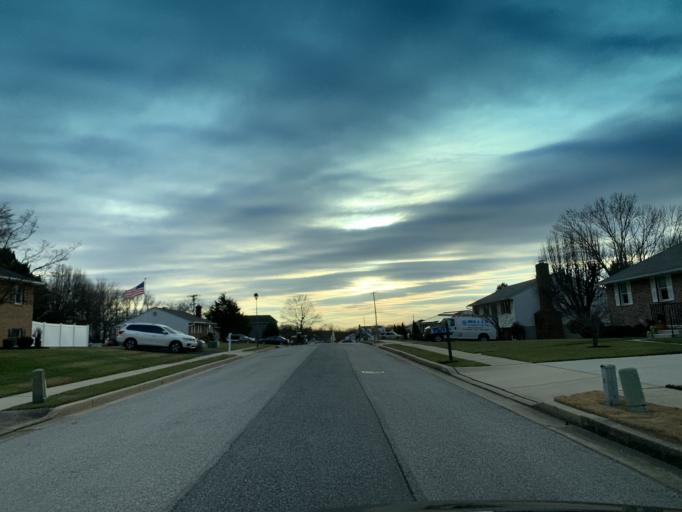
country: US
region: Maryland
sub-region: Baltimore County
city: Perry Hall
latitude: 39.4173
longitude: -76.4504
